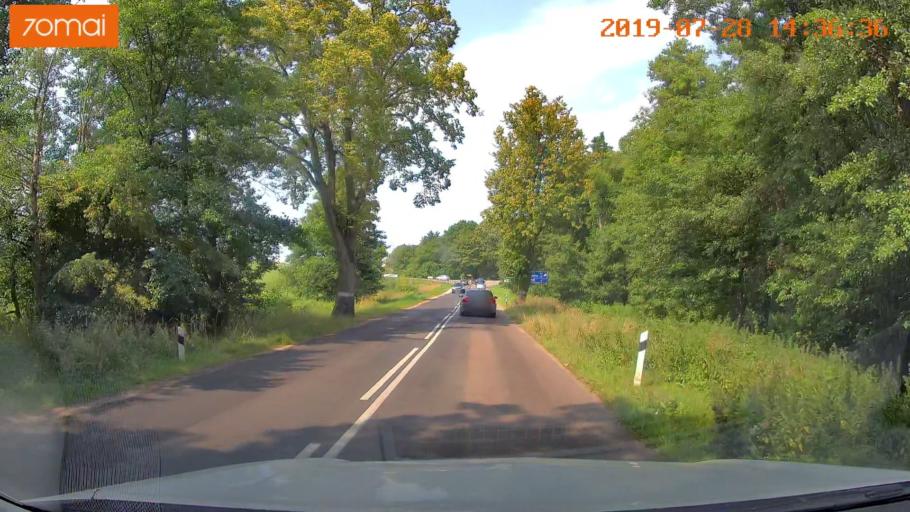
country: RU
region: Kaliningrad
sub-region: Gorod Kaliningrad
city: Yantarnyy
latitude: 54.8387
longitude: 20.0069
